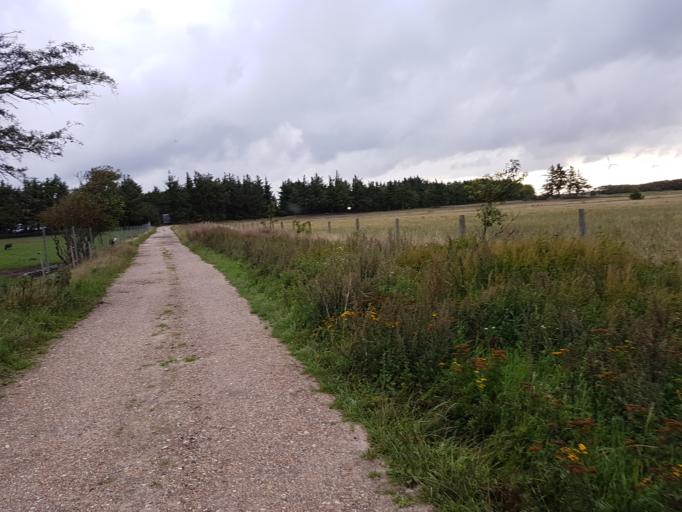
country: DK
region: Central Jutland
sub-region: Ringkobing-Skjern Kommune
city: Hvide Sande
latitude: 55.8526
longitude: 8.2922
